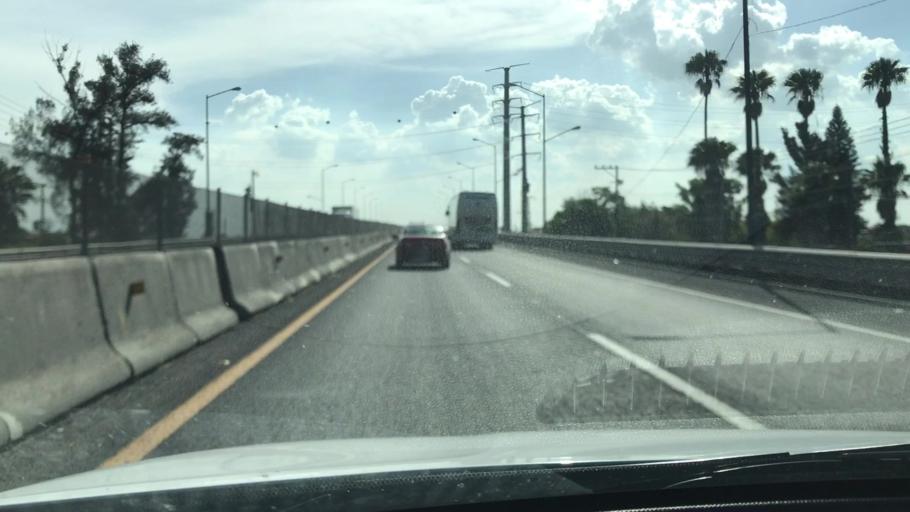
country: MX
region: Guanajuato
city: Villagran
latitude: 20.5088
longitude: -100.9881
